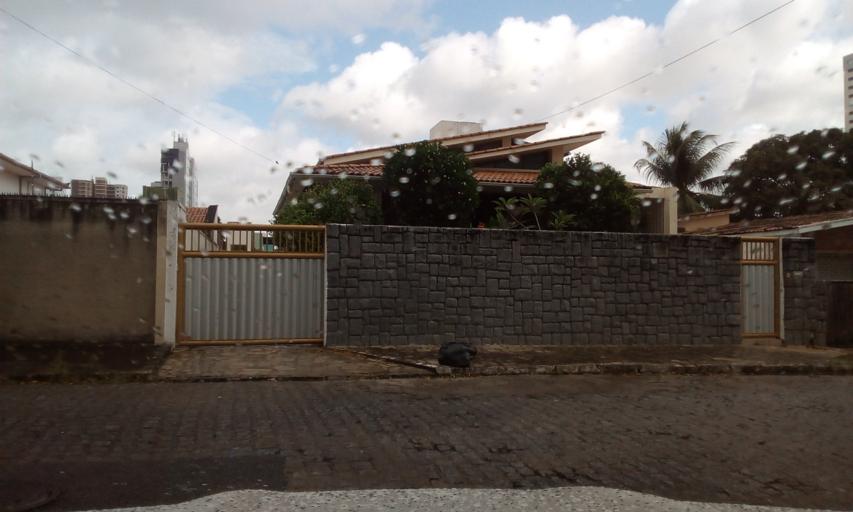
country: BR
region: Paraiba
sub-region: Joao Pessoa
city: Joao Pessoa
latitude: -7.1165
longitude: -34.8546
